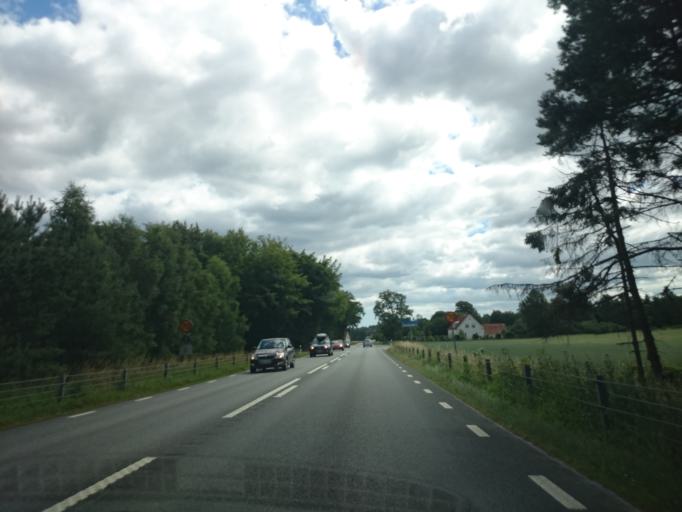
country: SE
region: Skane
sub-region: Kristianstads Kommun
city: Degeberga
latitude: 55.8153
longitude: 14.1321
